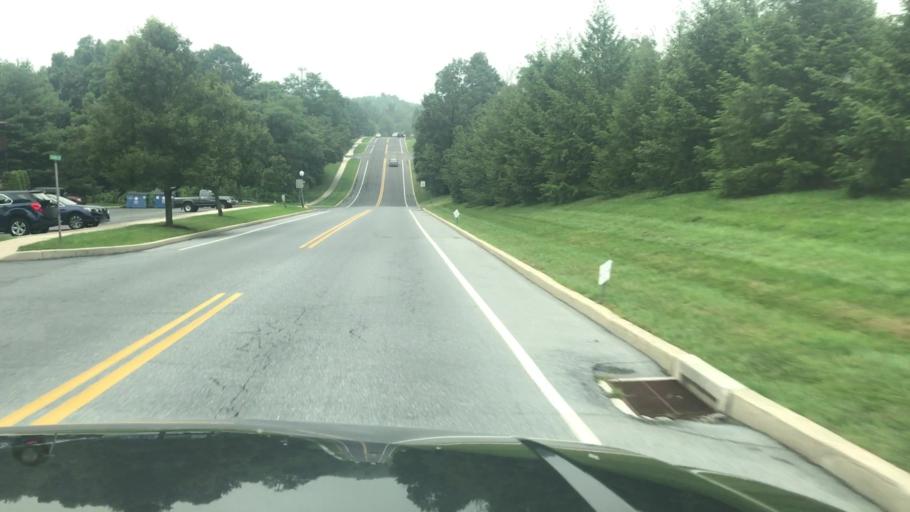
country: US
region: Pennsylvania
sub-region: Cumberland County
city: Enola
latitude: 40.2778
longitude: -76.9731
